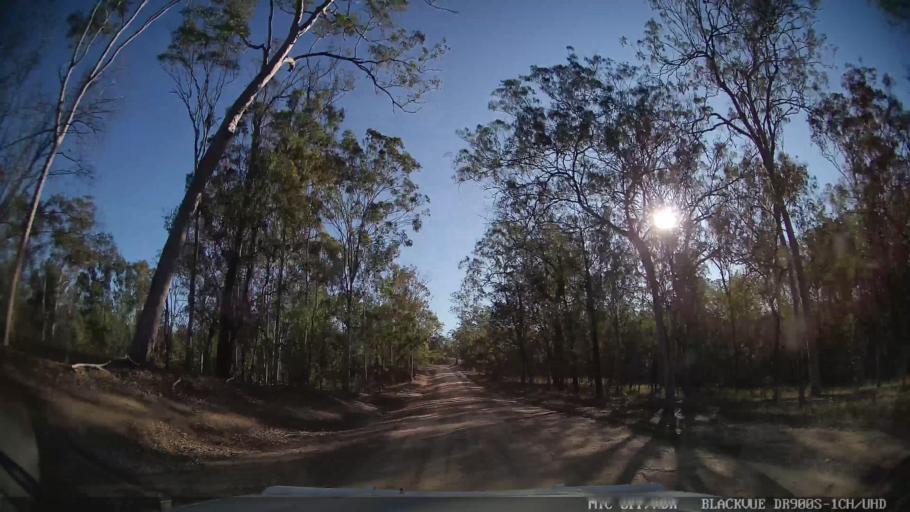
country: AU
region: Queensland
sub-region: Bundaberg
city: Sharon
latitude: -24.7362
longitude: 151.5205
